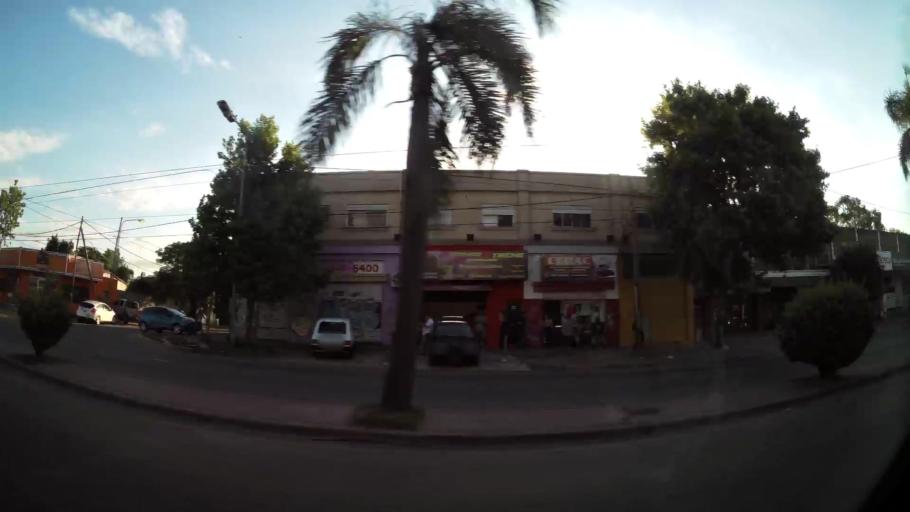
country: AR
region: Buenos Aires
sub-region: Partido de Tigre
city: Tigre
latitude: -34.4555
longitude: -58.6402
